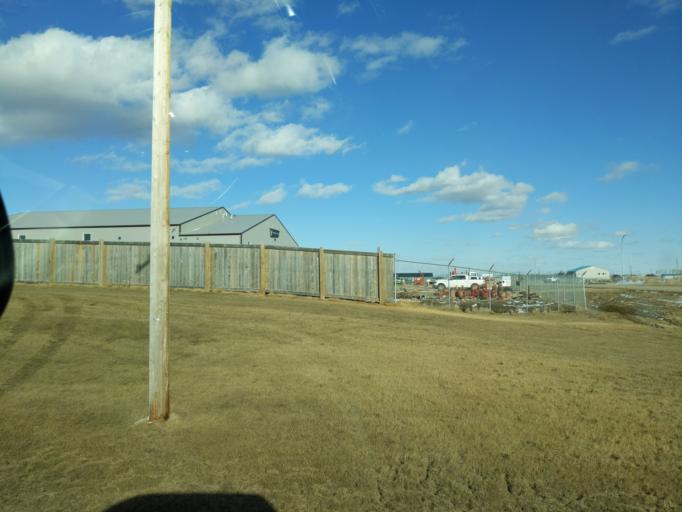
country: CA
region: Saskatchewan
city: Lloydminster
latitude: 53.2441
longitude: -109.9791
